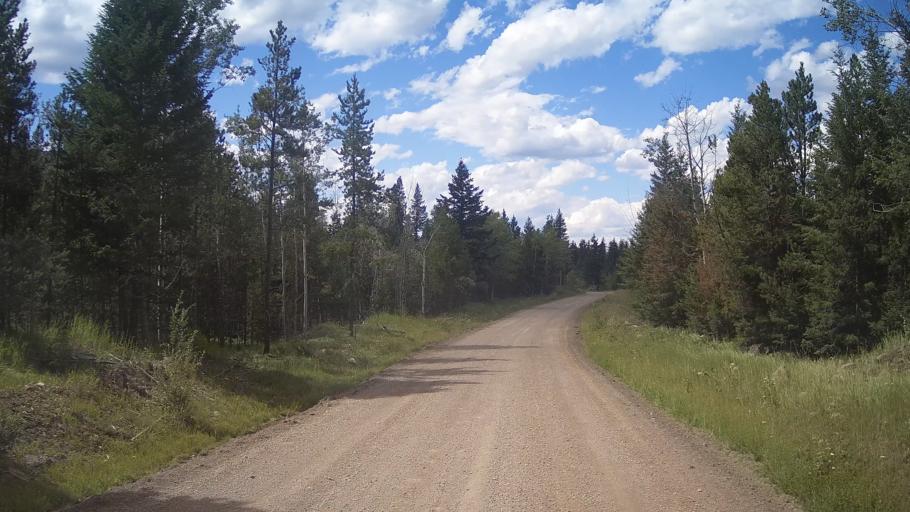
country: CA
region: British Columbia
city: Lillooet
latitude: 51.3234
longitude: -121.8699
